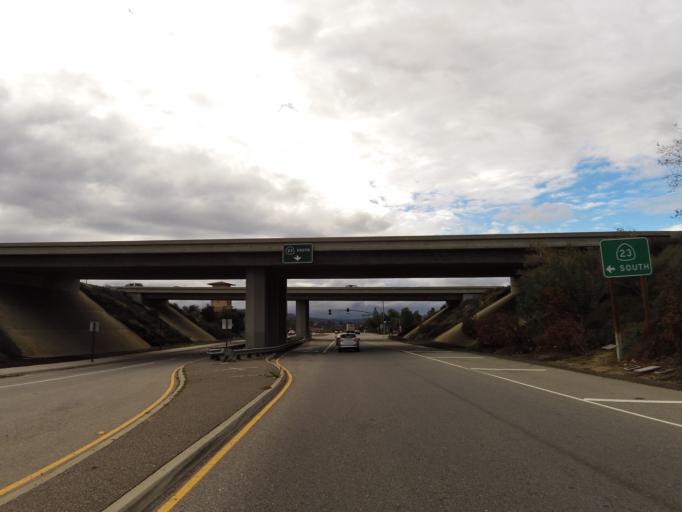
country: US
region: California
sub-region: Ventura County
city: Moorpark
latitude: 34.2827
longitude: -118.8625
